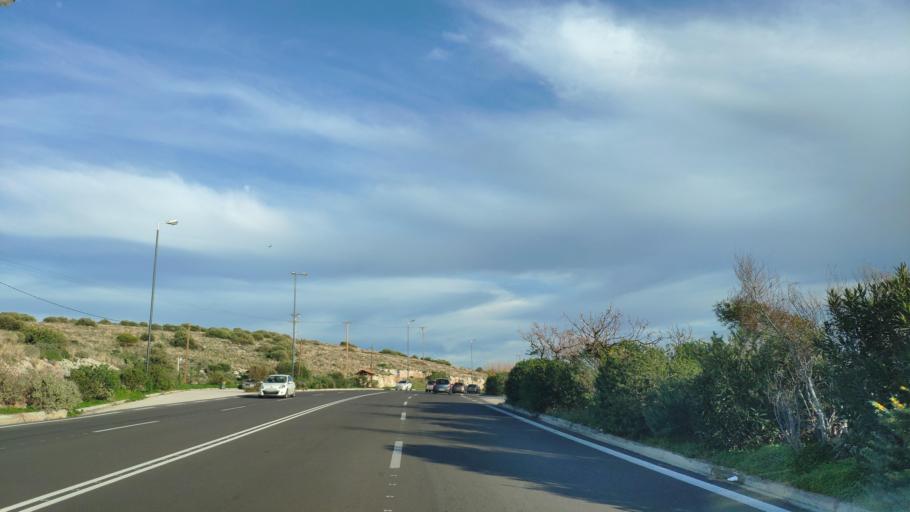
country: GR
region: Attica
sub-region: Nomarchia Anatolikis Attikis
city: Vouliagmeni
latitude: 37.7976
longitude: 23.7959
